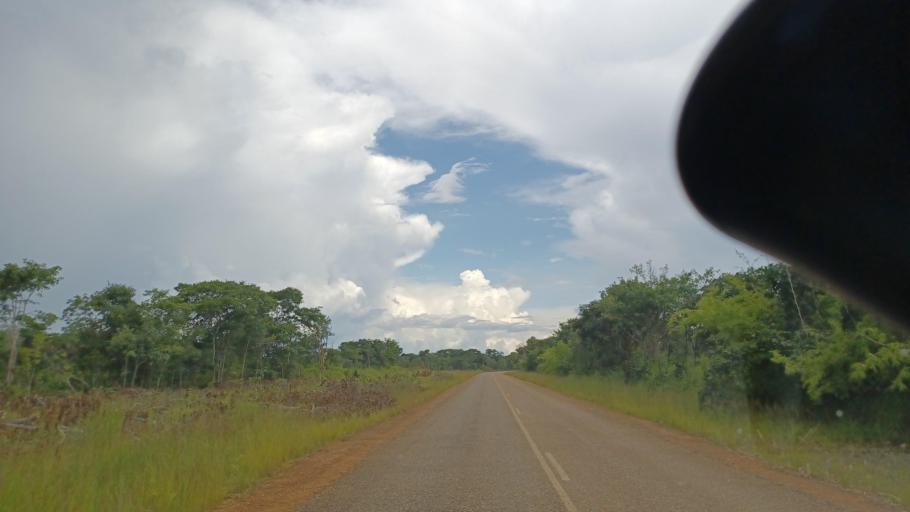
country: ZM
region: North-Western
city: Kasempa
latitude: -13.1291
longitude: 25.8748
